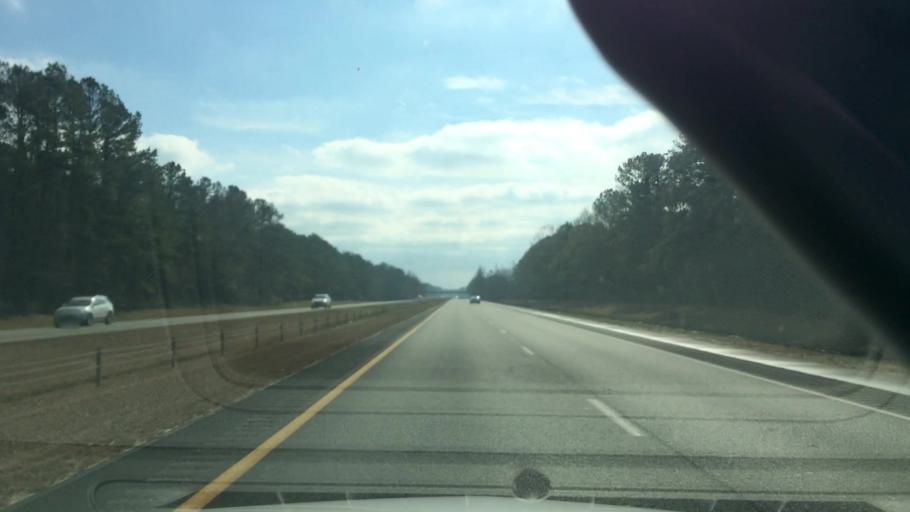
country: US
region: North Carolina
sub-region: Pender County
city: Rocky Point
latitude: 34.4899
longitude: -77.8778
